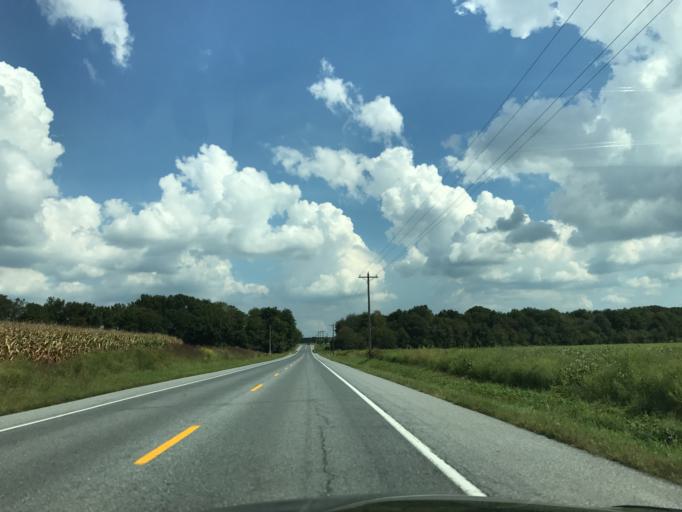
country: US
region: Maryland
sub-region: Queen Anne's County
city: Kingstown
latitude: 39.1905
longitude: -75.8372
